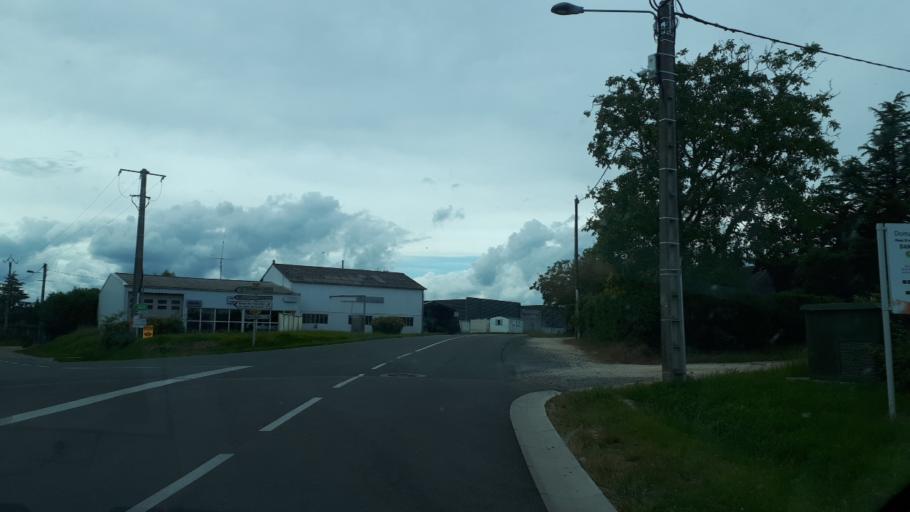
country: FR
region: Centre
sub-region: Departement de l'Indre
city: Reuilly
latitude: 47.0889
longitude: 2.0344
